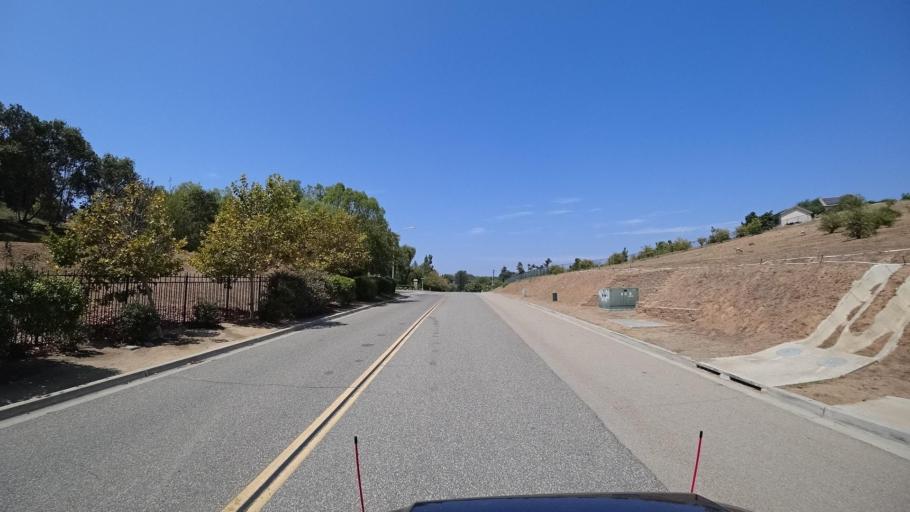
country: US
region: California
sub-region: San Diego County
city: Bonsall
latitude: 33.3244
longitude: -117.2120
